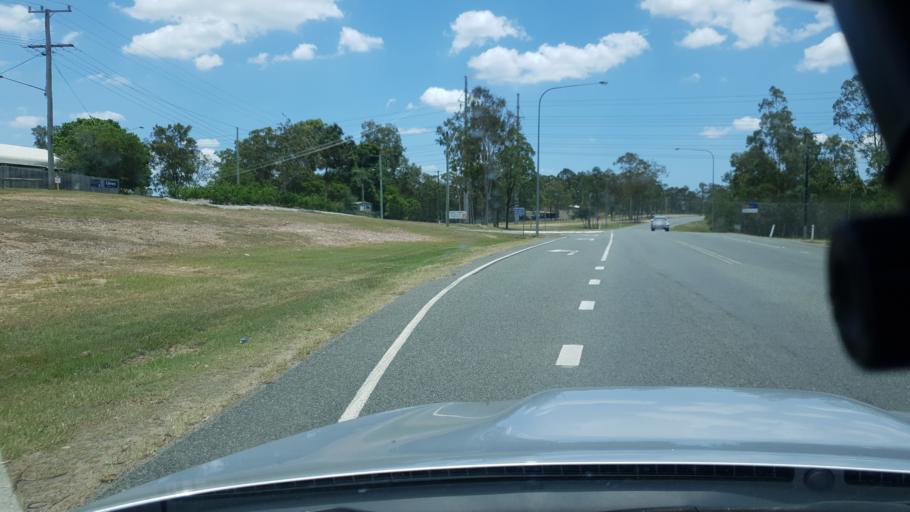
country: AU
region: Queensland
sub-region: Logan
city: North Maclean
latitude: -27.7309
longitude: 152.9843
